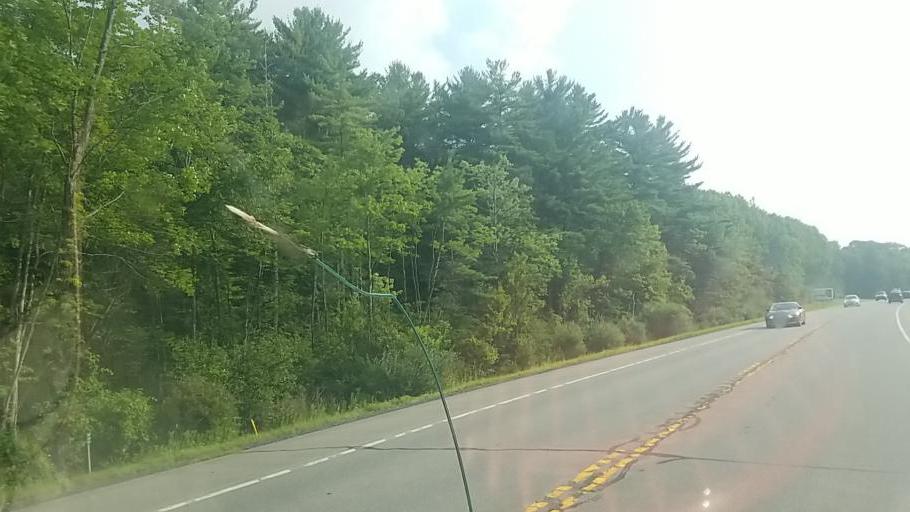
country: US
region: New York
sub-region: Fulton County
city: Gloversville
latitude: 43.0378
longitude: -74.3389
